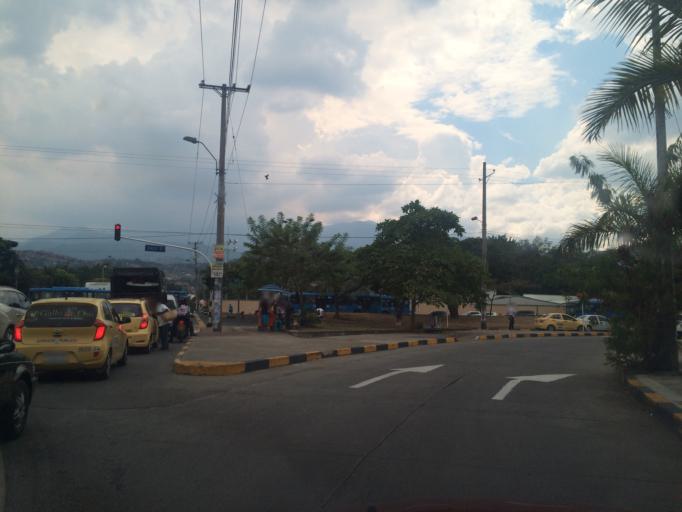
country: CO
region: Valle del Cauca
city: Cali
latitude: 3.3863
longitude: -76.5440
